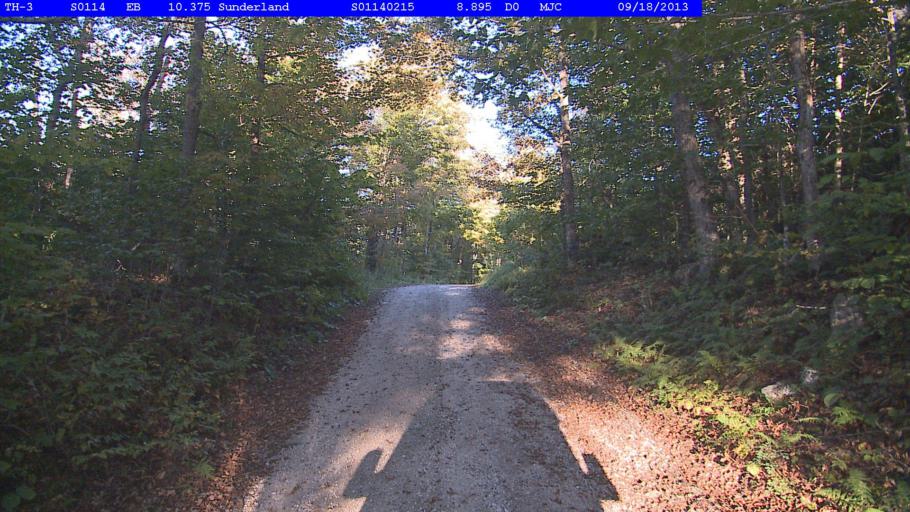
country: US
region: Vermont
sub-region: Bennington County
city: Manchester Center
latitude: 43.0557
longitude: -73.0163
